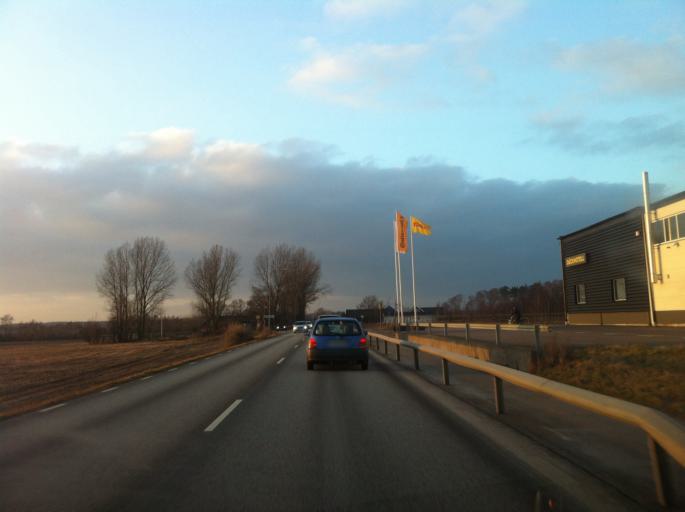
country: SE
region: Skane
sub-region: Kavlinge Kommun
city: Loddekopinge
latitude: 55.7880
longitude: 13.0023
